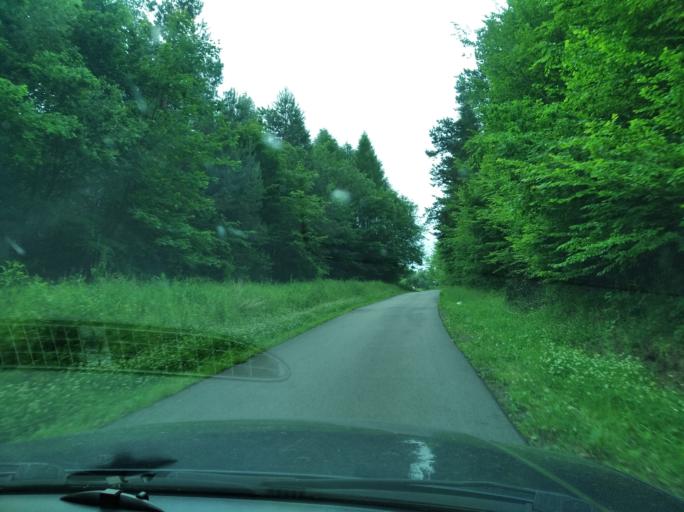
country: PL
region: Subcarpathian Voivodeship
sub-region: Powiat przemyski
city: Dubiecko
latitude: 49.8709
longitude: 22.4051
